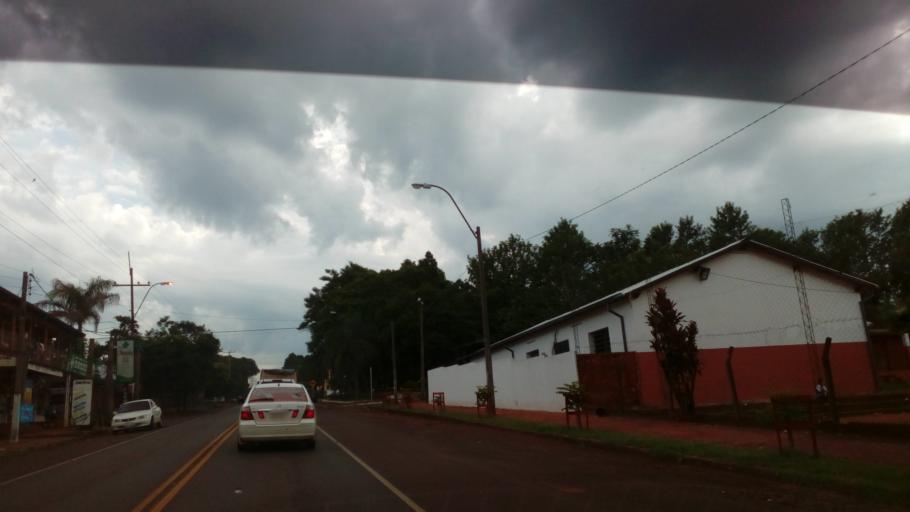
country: PY
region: Itapua
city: Obligado
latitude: -27.0836
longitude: -55.6493
